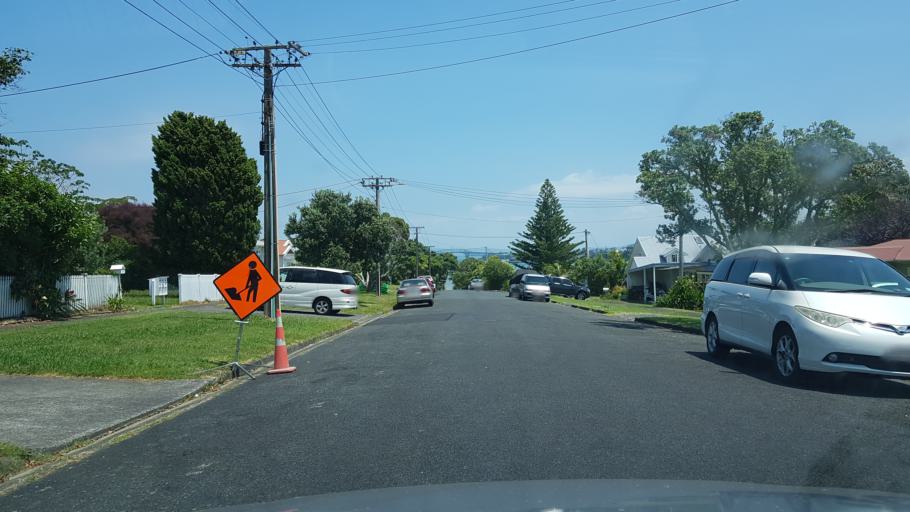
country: NZ
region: Auckland
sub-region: Auckland
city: North Shore
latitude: -36.8166
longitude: 174.7871
